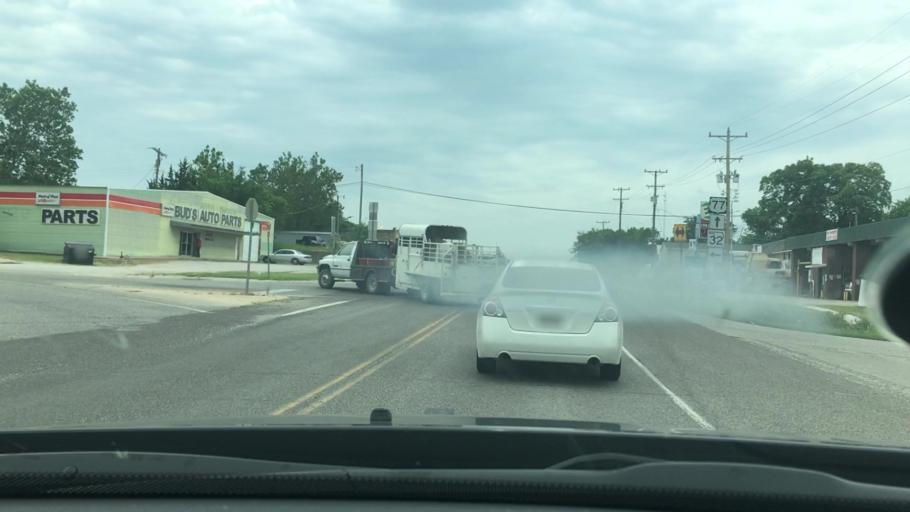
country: US
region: Oklahoma
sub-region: Love County
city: Marietta
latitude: 33.9382
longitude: -97.1263
